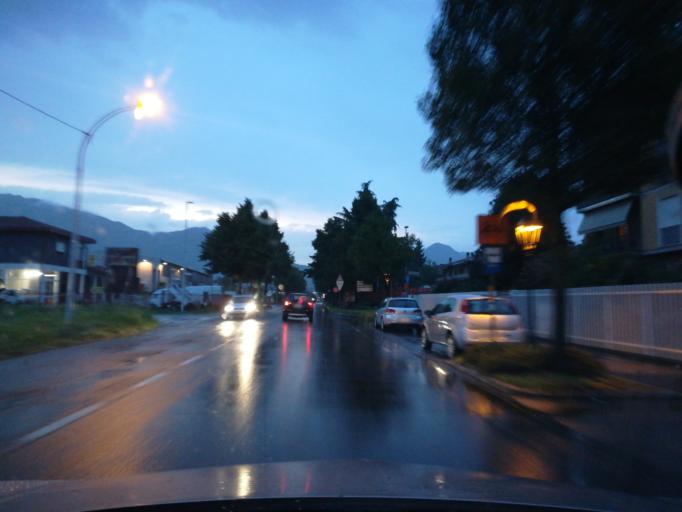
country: IT
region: Lombardy
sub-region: Provincia di Bergamo
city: Almenno San Bartolomeo
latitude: 45.7285
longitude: 9.5834
